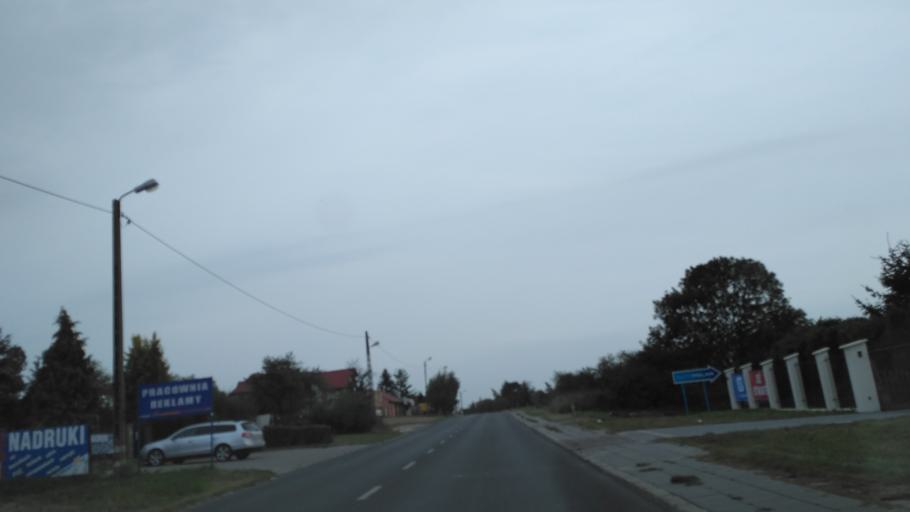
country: PL
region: Lublin Voivodeship
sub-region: Powiat lubelski
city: Lublin
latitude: 51.2172
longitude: 22.5902
